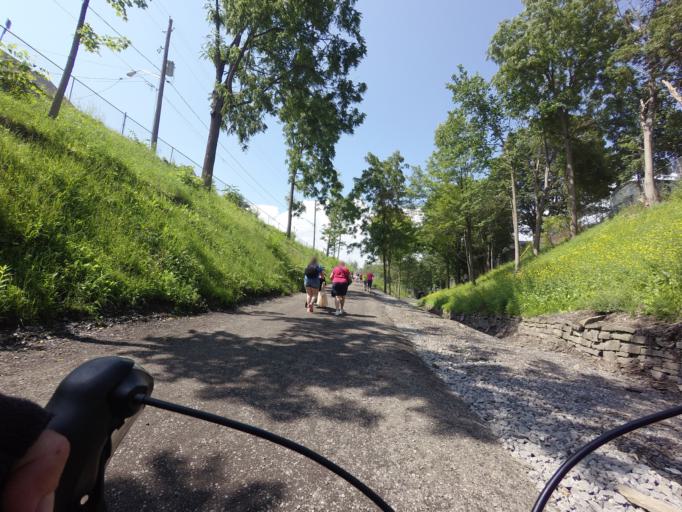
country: CA
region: Ontario
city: Brockville
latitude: 44.5935
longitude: -75.6866
